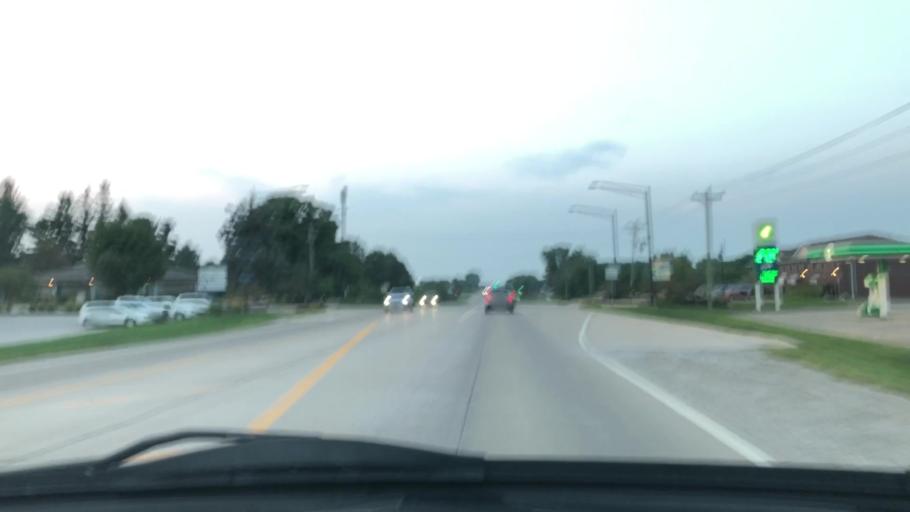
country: US
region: Iowa
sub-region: Johnson County
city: North Liberty
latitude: 41.7338
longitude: -91.6076
